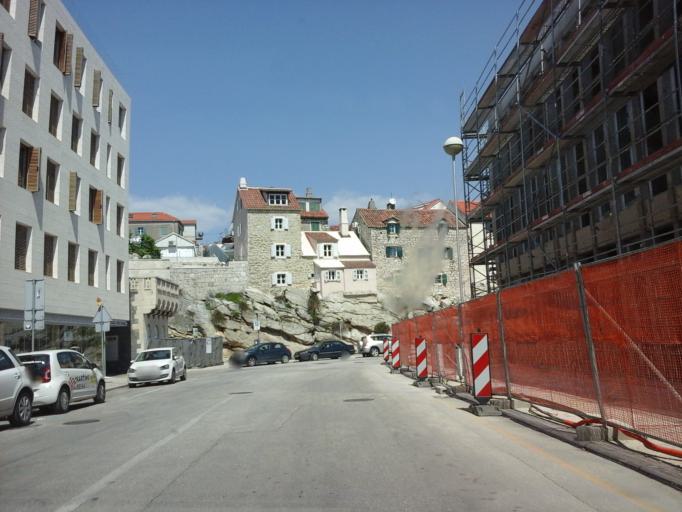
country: HR
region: Splitsko-Dalmatinska
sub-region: Grad Split
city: Split
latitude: 43.5067
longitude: 16.4326
